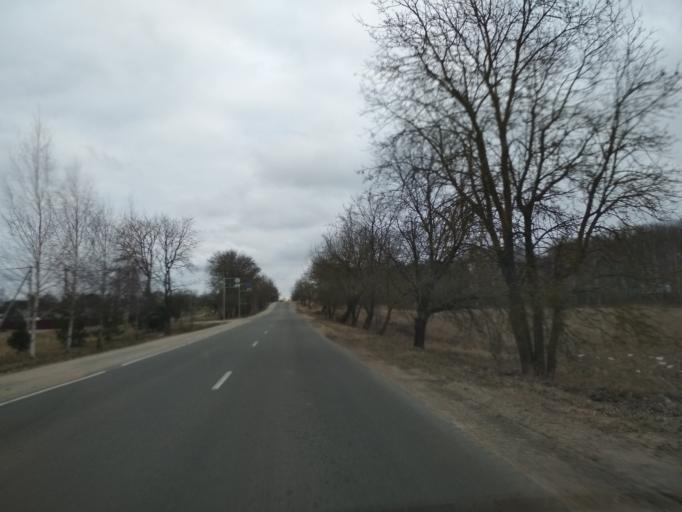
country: BY
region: Minsk
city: Druzhny
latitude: 53.5718
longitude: 27.9507
